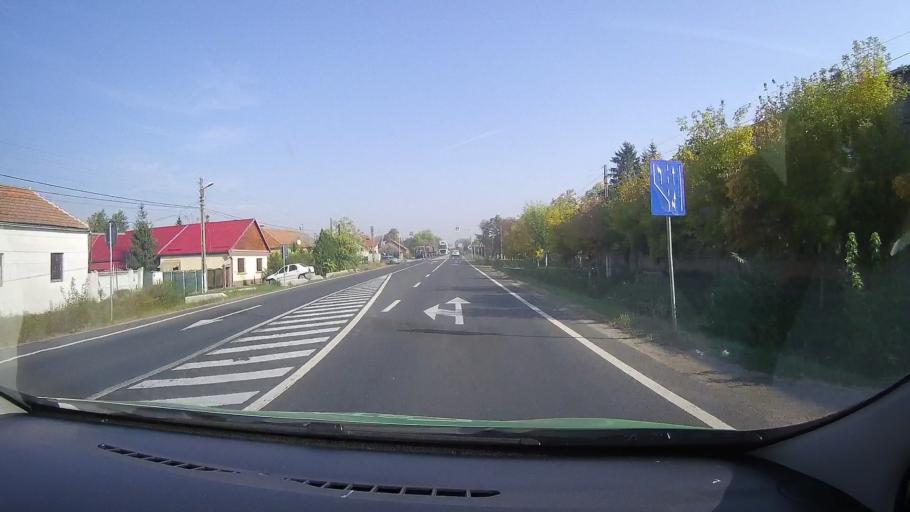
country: RO
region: Arad
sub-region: Comuna Zerind
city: Zerind
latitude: 46.6263
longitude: 21.5175
